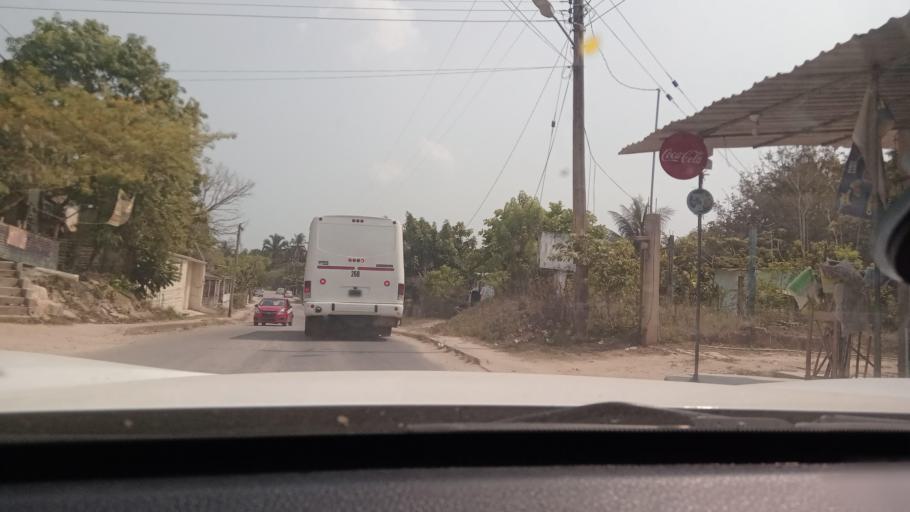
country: MX
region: Veracruz
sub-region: Minatitlan
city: Las Lomas
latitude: 17.9665
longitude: -94.5649
